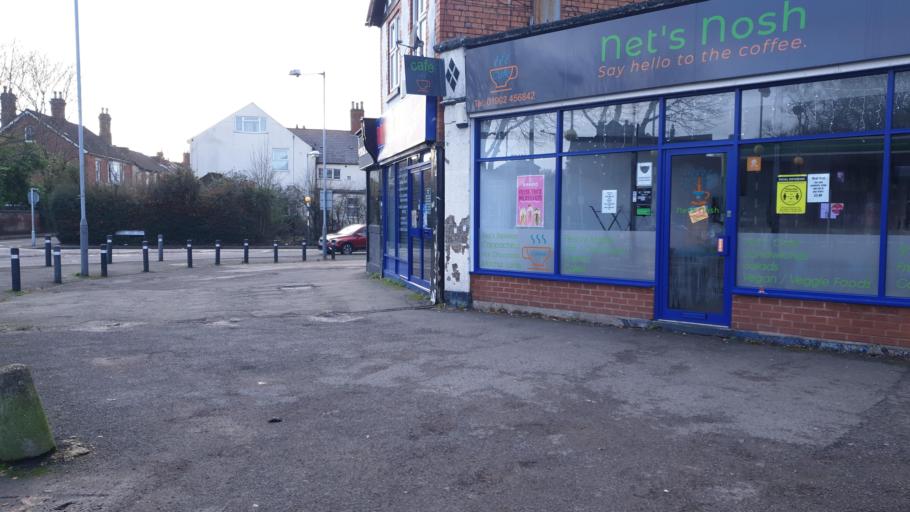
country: GB
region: England
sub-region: Wolverhampton
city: Wolverhampton
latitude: 52.5718
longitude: -2.1453
